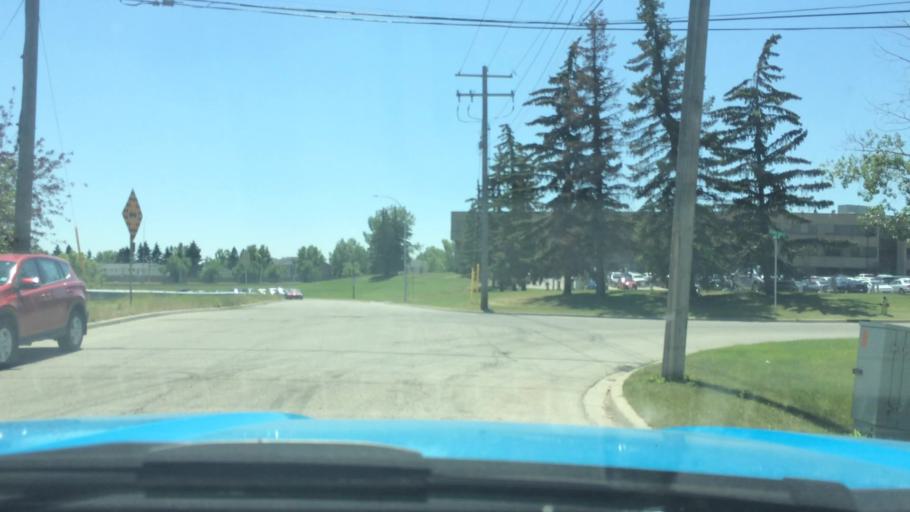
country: CA
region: Alberta
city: Calgary
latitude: 51.0526
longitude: -113.9896
